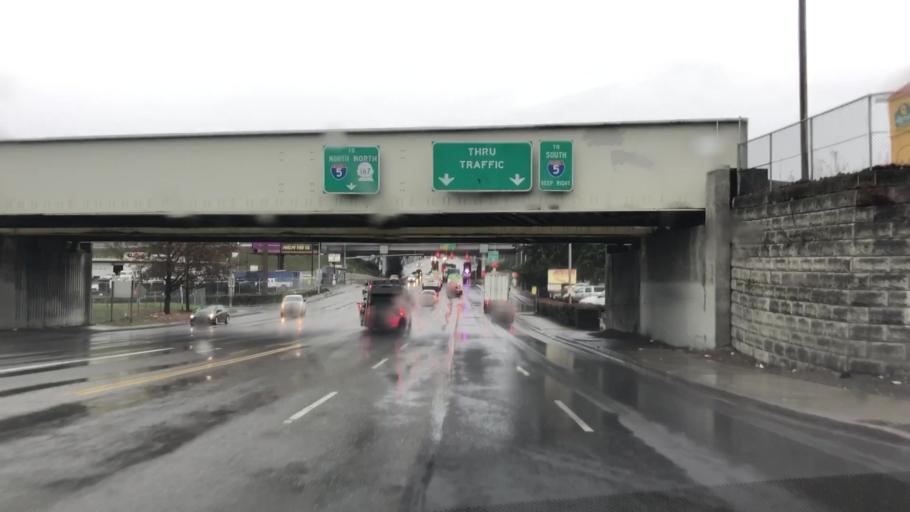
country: US
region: Washington
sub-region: Pierce County
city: Tacoma
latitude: 47.2415
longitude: -122.4112
